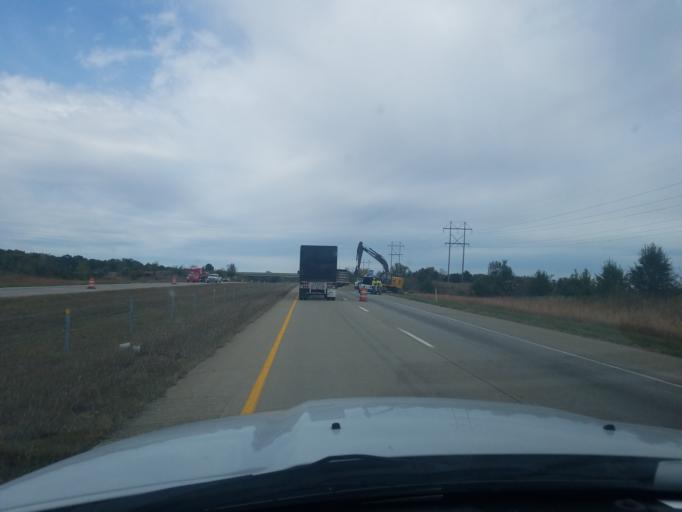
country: US
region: Indiana
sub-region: Gibson County
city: Haubstadt
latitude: 38.1477
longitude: -87.4726
